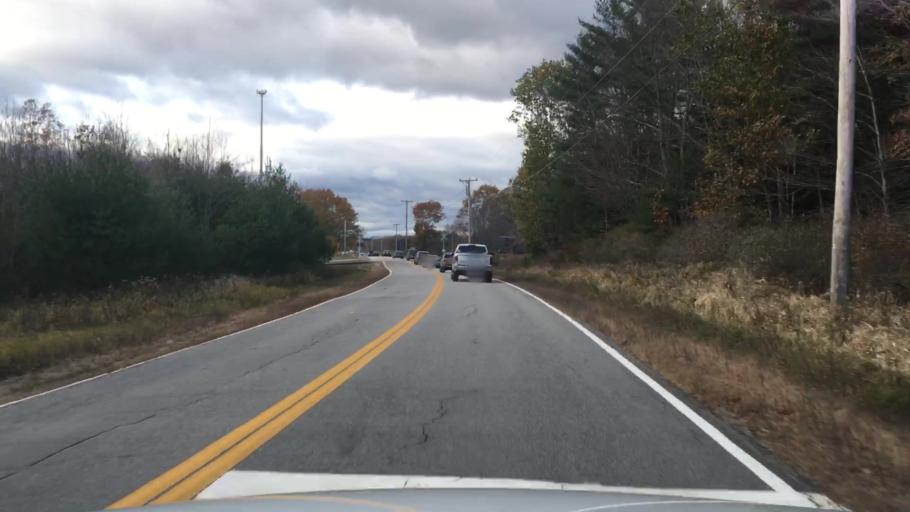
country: US
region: Maine
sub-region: Androscoggin County
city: Leeds
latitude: 44.3306
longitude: -70.1241
